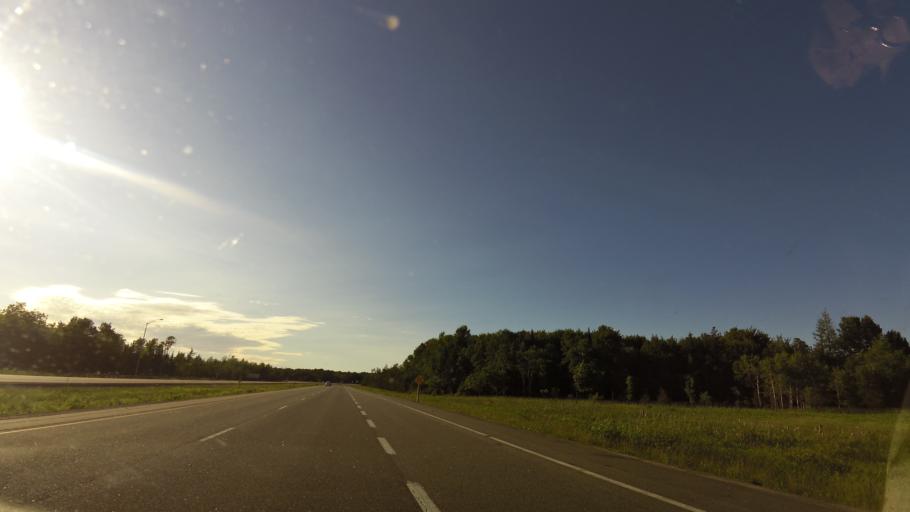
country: CA
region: Ontario
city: Barrie
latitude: 44.5247
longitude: -79.7411
